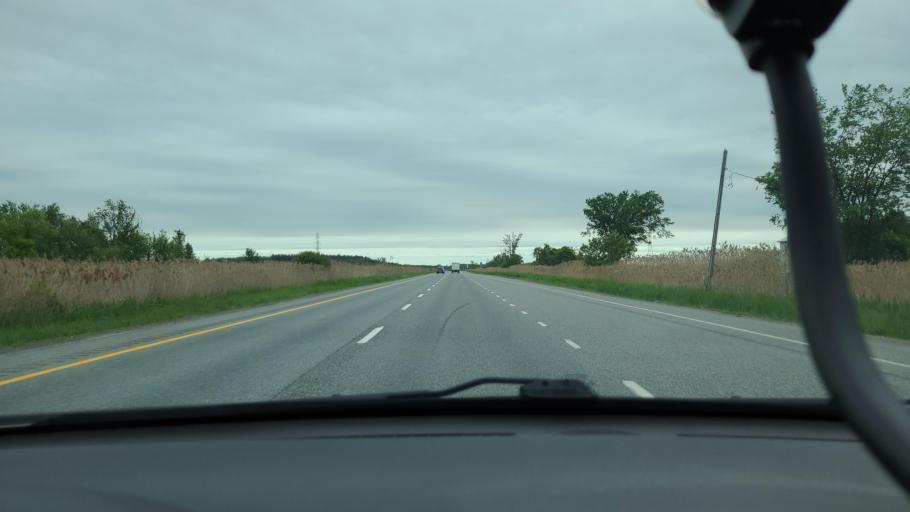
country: CA
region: Quebec
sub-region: Lanaudiere
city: Mascouche
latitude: 45.7539
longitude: -73.5854
